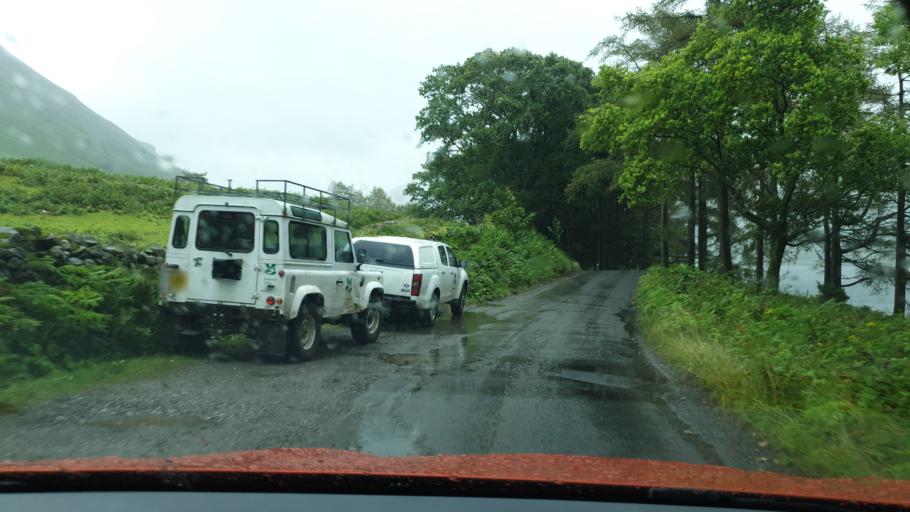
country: GB
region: England
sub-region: Cumbria
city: Seascale
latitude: 54.4491
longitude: -3.2880
